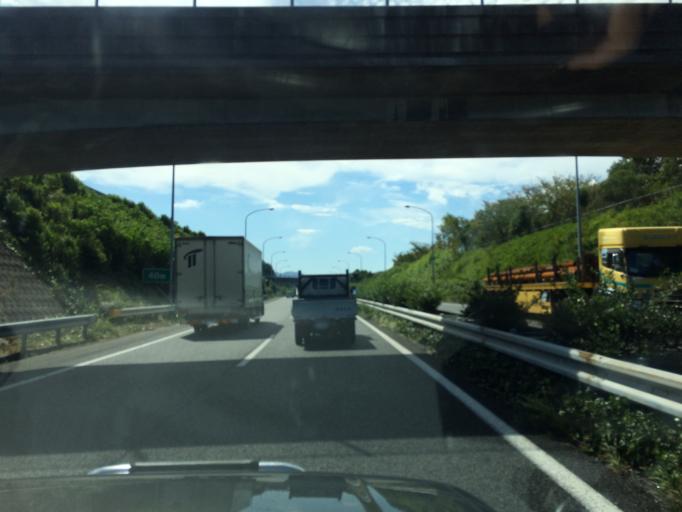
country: JP
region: Osaka
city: Izumi
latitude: 34.4866
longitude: 135.4654
